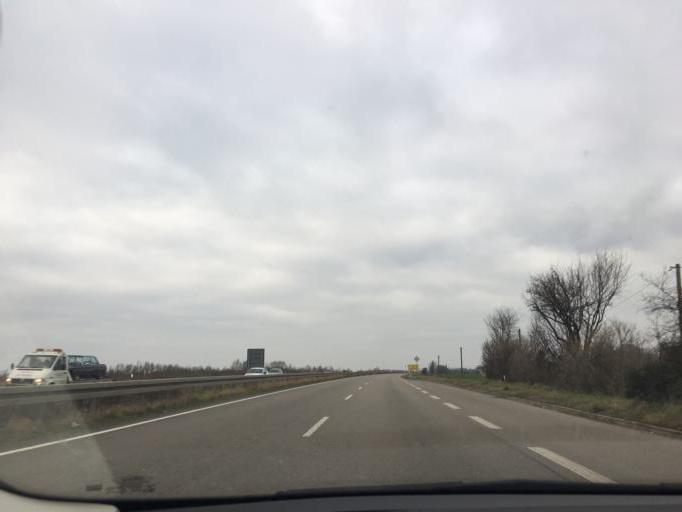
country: DE
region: Saxony
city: Borna
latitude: 51.1587
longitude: 12.5044
